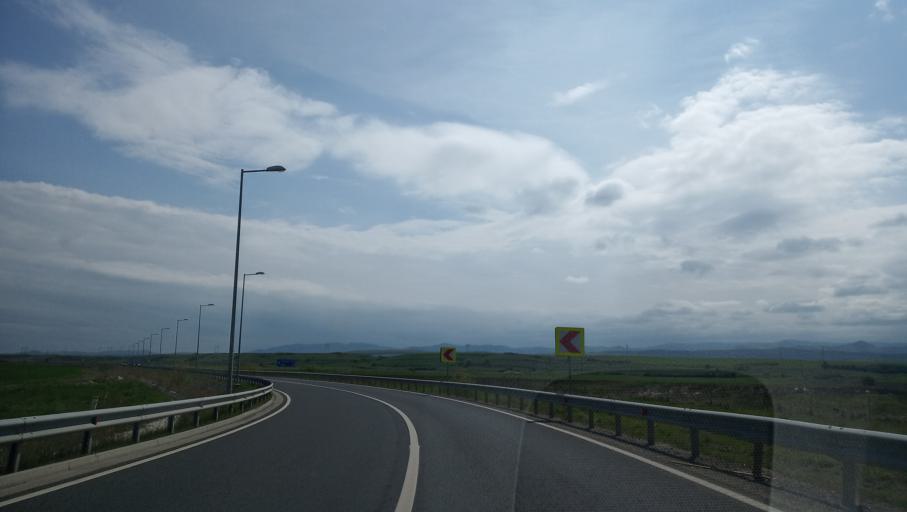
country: RO
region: Hunedoara
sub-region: Comuna Romos
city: Romos
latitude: 45.8875
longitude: 23.2575
